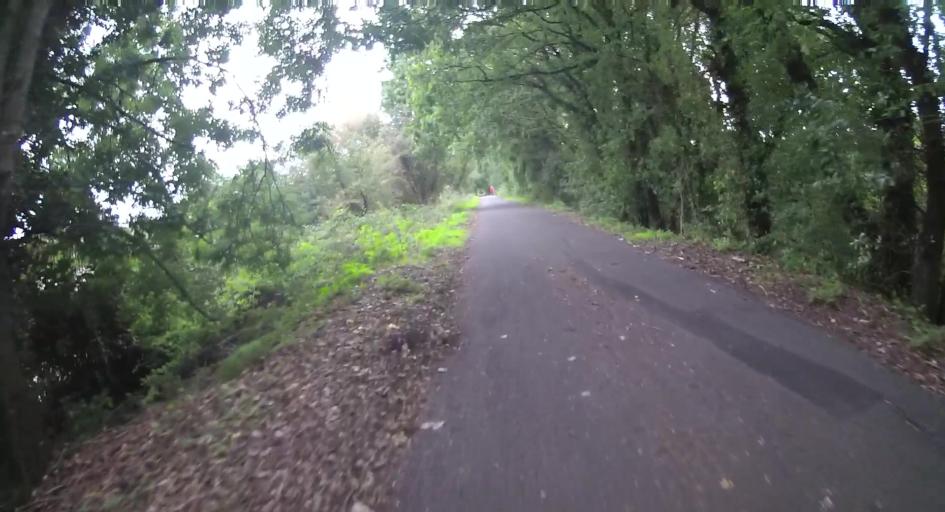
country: GB
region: England
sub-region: Isle of Wight
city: East Cowes
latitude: 50.7463
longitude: -1.2937
